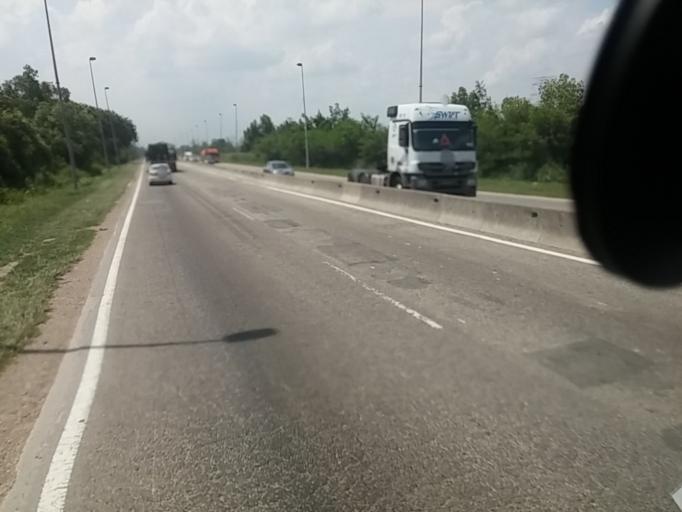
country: MY
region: Selangor
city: Klang
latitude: 2.9814
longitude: 101.3725
